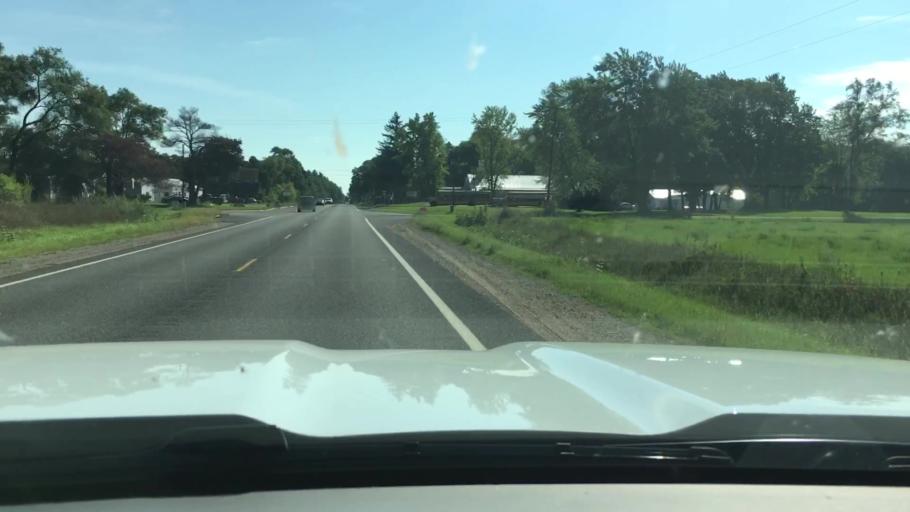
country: US
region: Michigan
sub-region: Montcalm County
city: Edmore
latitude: 43.4083
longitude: -84.8666
